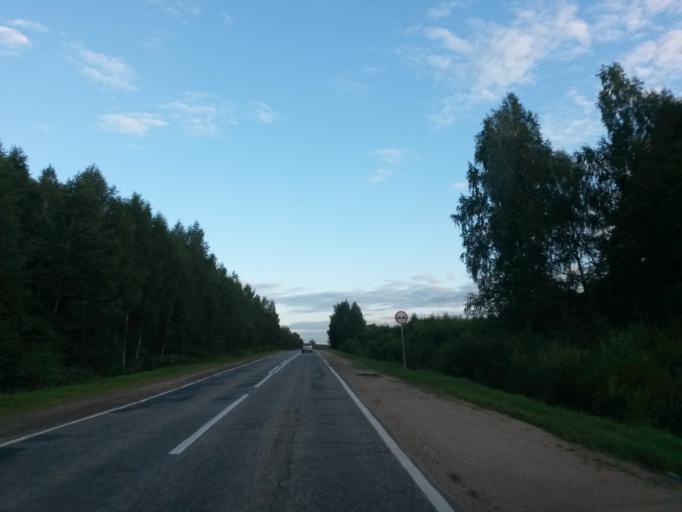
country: RU
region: Jaroslavl
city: Krasnyye Tkachi
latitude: 57.4545
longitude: 39.9116
